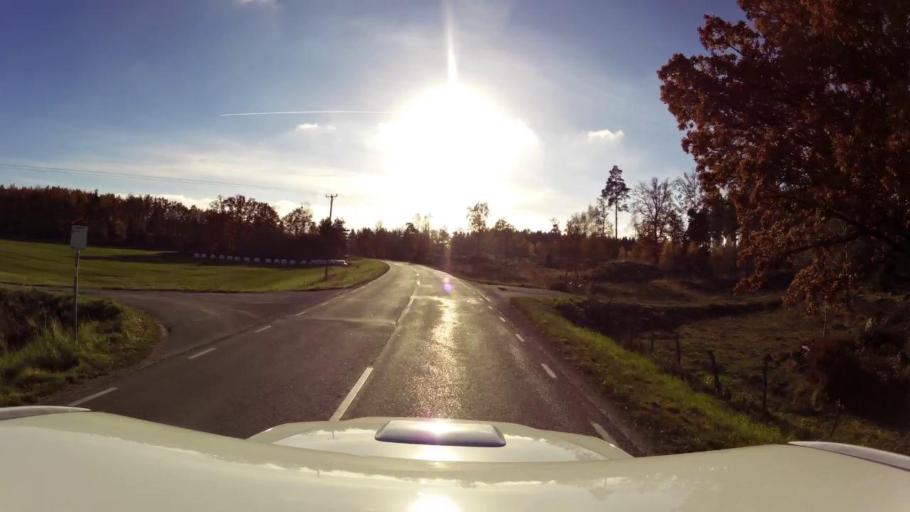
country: SE
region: OEstergoetland
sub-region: Linkopings Kommun
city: Vikingstad
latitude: 58.3138
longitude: 15.4911
